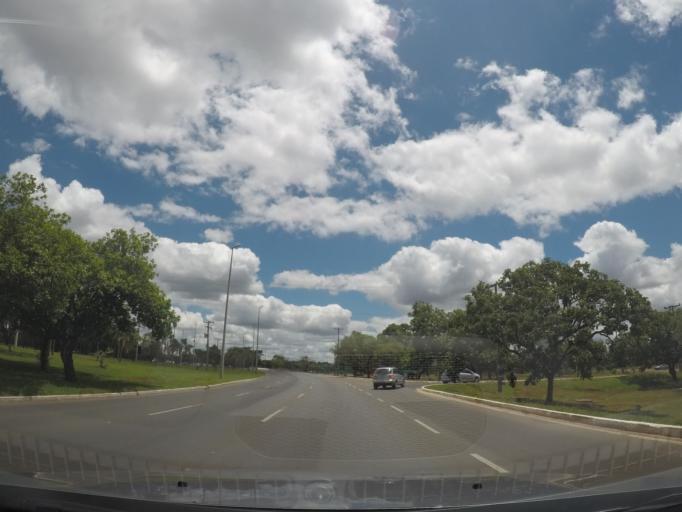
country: BR
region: Federal District
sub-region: Brasilia
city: Brasilia
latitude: -15.8069
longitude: -47.8560
